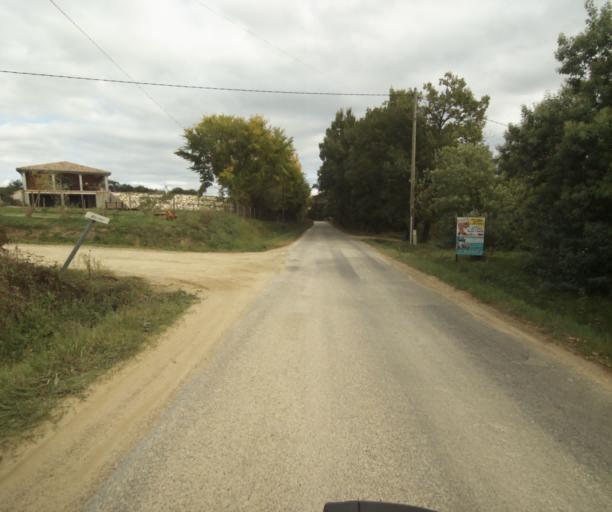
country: FR
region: Midi-Pyrenees
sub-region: Departement du Tarn-et-Garonne
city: Verdun-sur-Garonne
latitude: 43.8579
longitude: 1.1295
